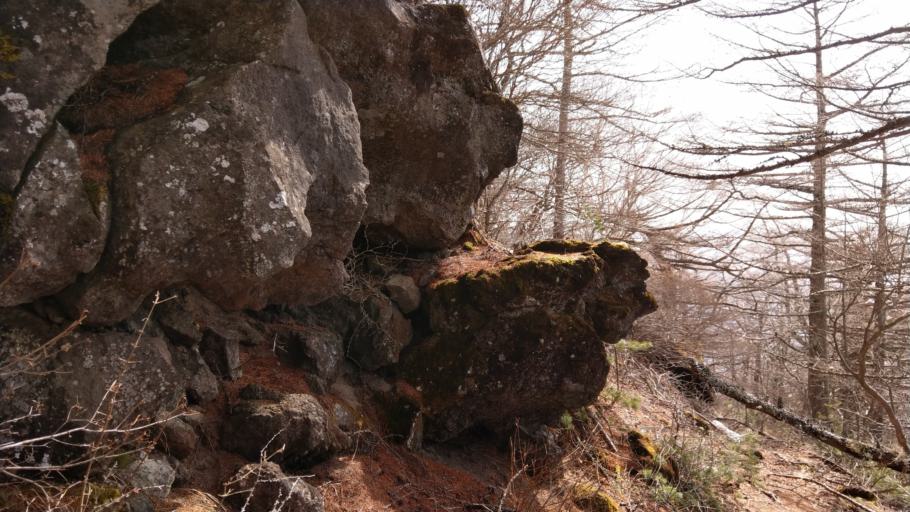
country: JP
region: Nagano
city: Komoro
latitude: 36.3944
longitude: 138.4529
